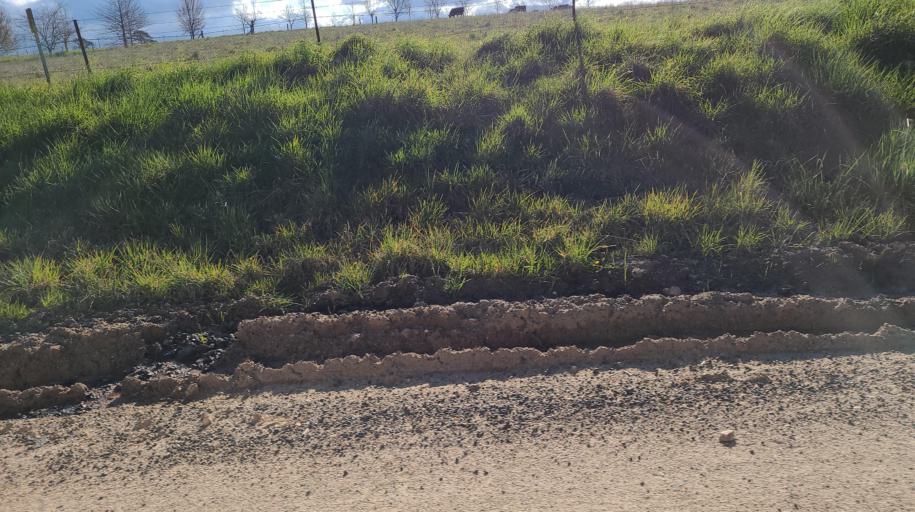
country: AU
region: New South Wales
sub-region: Blayney
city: Millthorpe
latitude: -33.4042
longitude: 149.3077
